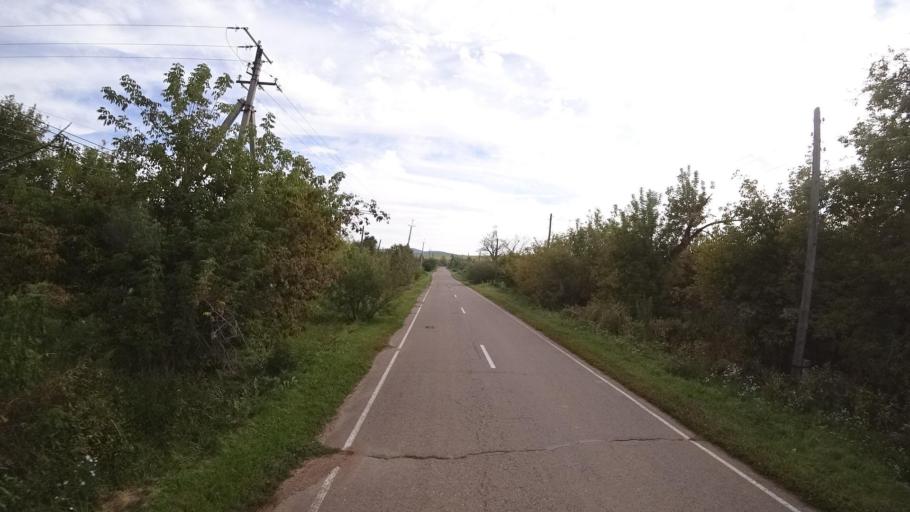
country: RU
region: Primorskiy
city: Dostoyevka
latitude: 44.3247
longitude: 133.4766
